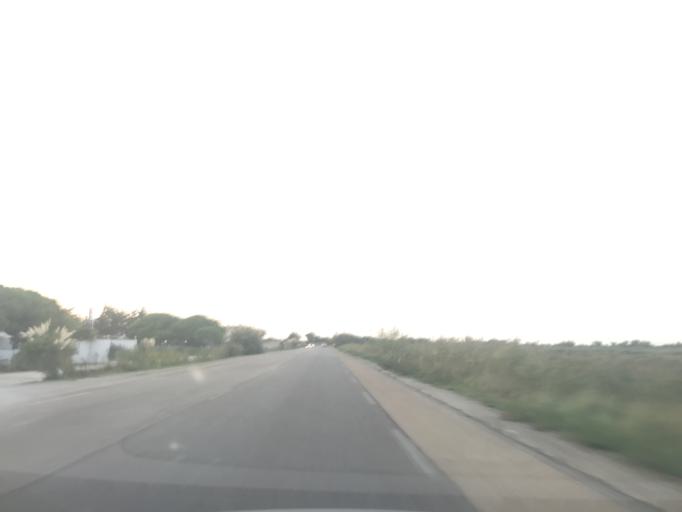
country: FR
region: Provence-Alpes-Cote d'Azur
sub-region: Departement des Bouches-du-Rhone
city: Saintes-Maries-de-la-Mer
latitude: 43.4736
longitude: 4.4109
